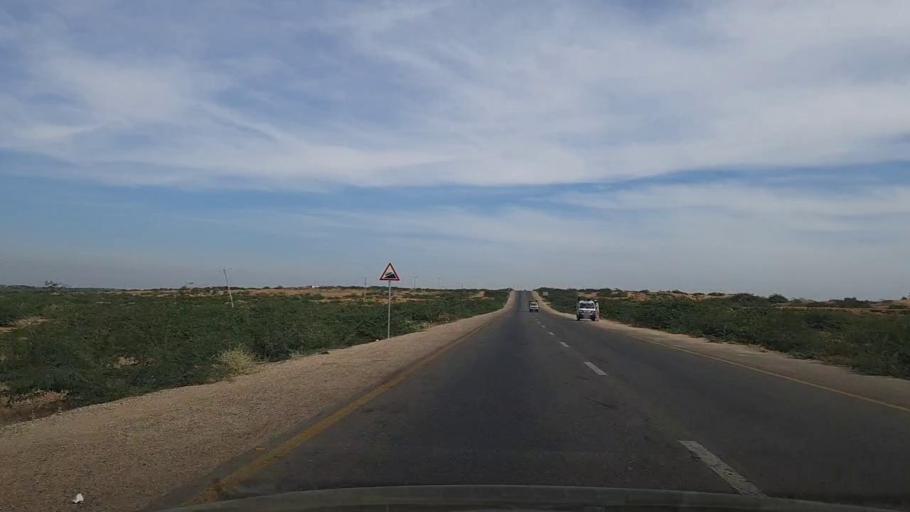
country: PK
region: Sindh
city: Thatta
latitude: 24.8475
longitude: 68.0124
